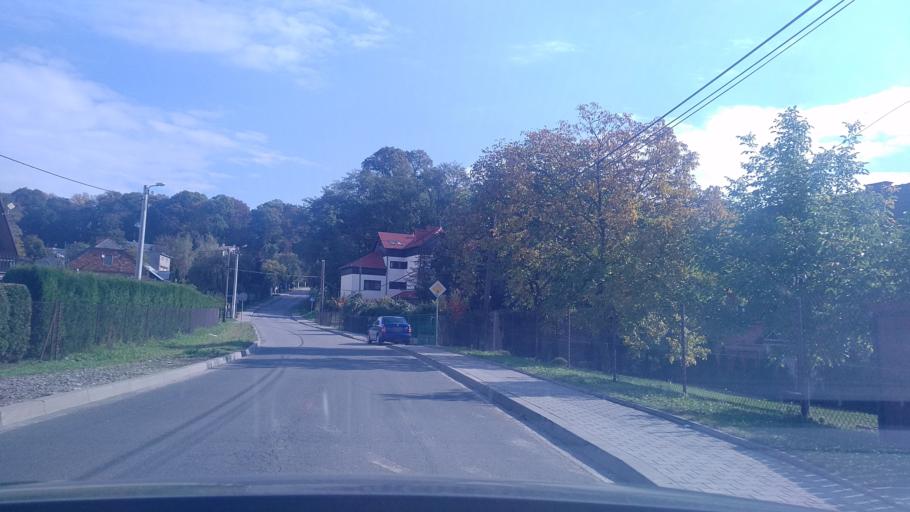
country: PL
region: Lesser Poland Voivodeship
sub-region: Powiat krakowski
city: Modlnica
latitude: 50.1325
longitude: 19.8597
